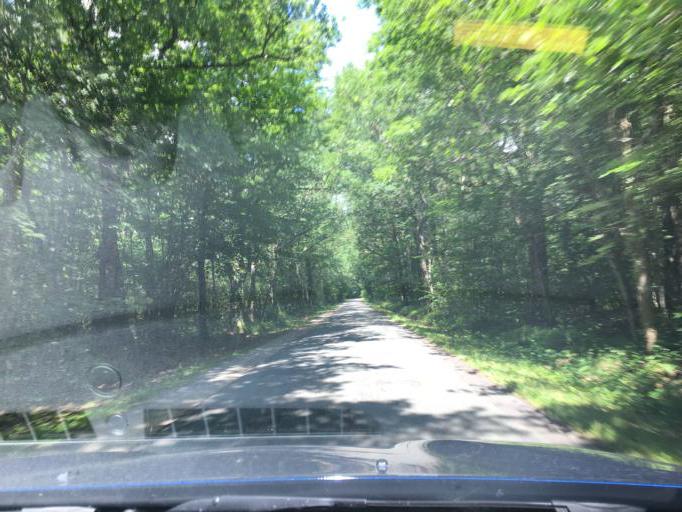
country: FR
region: Centre
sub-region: Departement du Loiret
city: Chevilly
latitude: 48.0158
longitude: 1.9250
